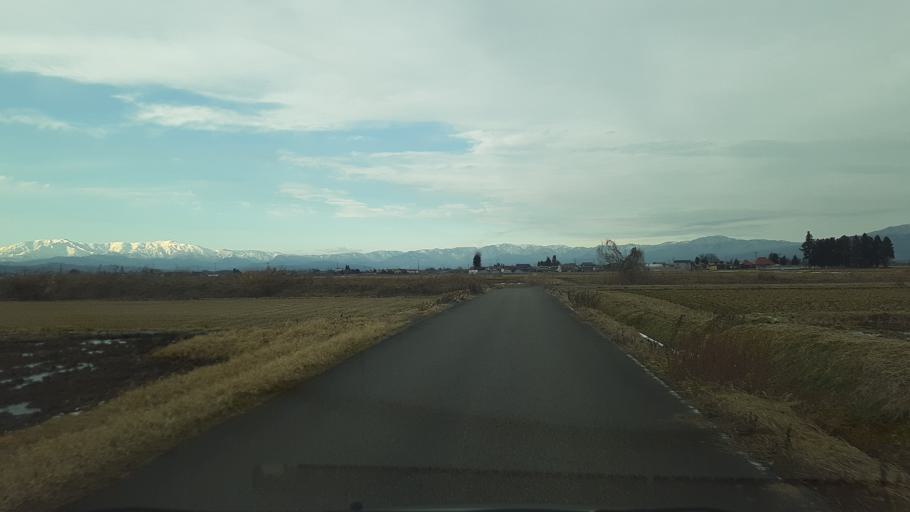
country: JP
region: Fukushima
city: Kitakata
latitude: 37.4720
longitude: 139.8474
